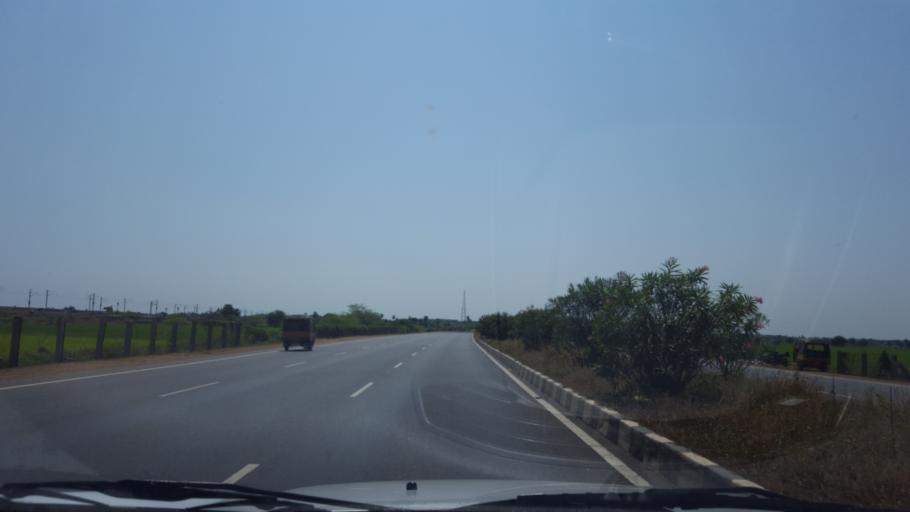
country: IN
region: Andhra Pradesh
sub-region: Prakasam
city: Singarayakonda
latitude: 15.1044
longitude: 80.0082
